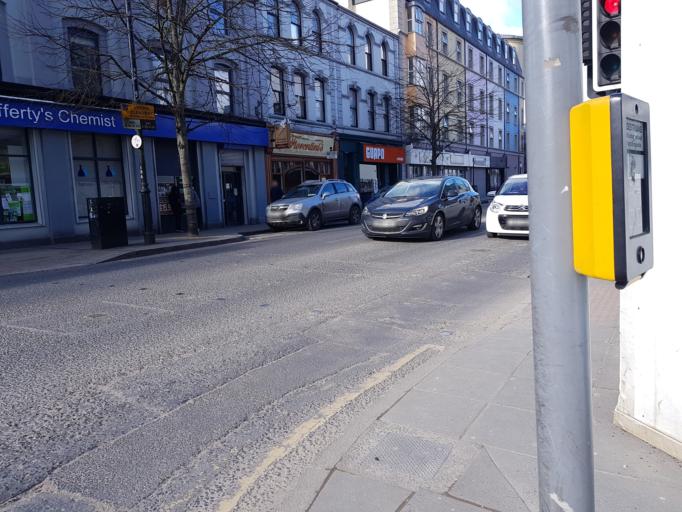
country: GB
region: Northern Ireland
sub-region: City of Derry
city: Derry
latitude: 55.0008
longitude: -7.3223
